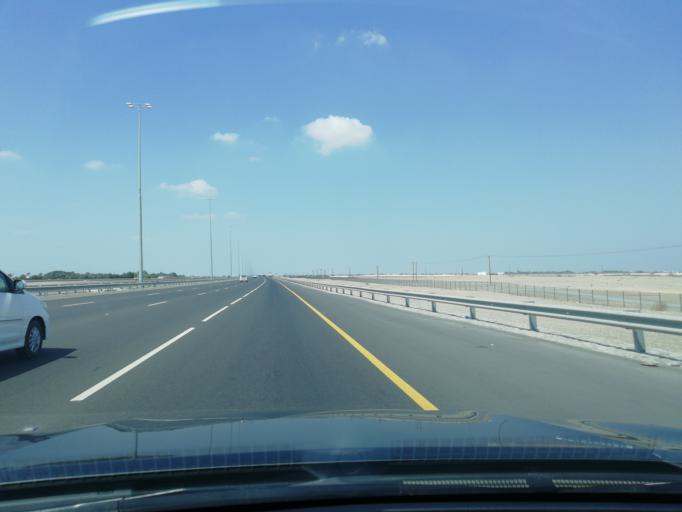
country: OM
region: Al Batinah
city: Barka'
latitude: 23.6261
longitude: 57.9491
